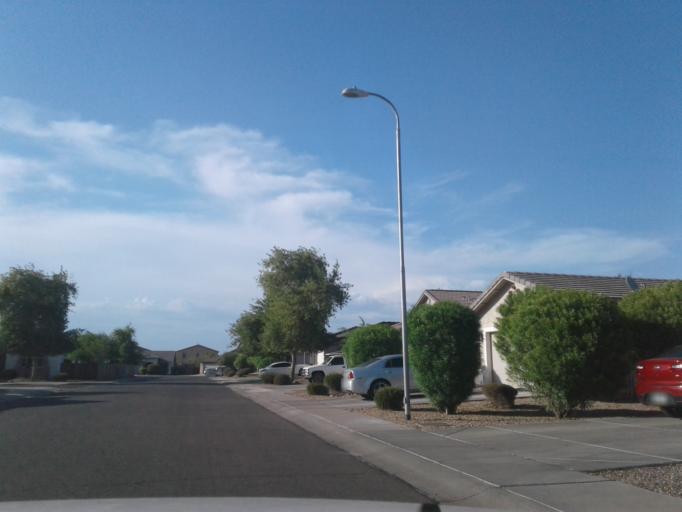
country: US
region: Arizona
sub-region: Maricopa County
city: Laveen
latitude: 33.3793
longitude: -112.2159
